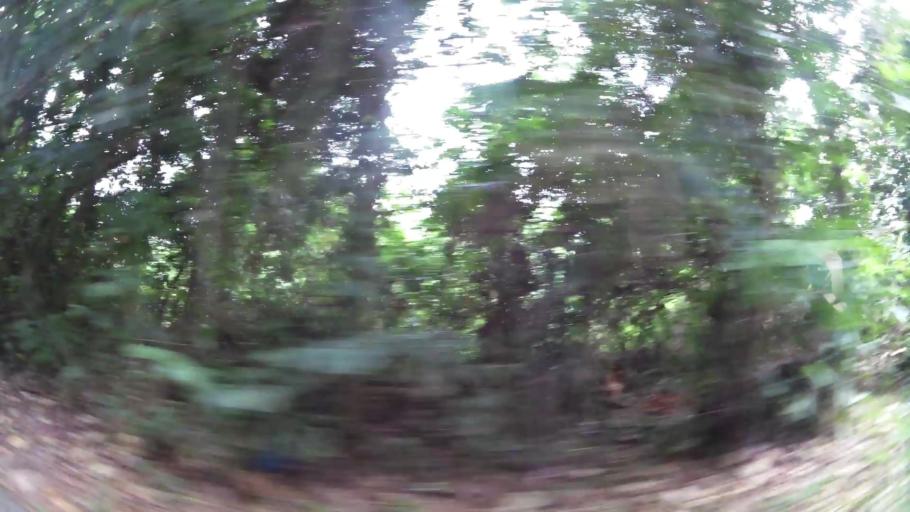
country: MY
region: Johor
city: Johor Bahru
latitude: 1.4440
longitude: 103.7078
